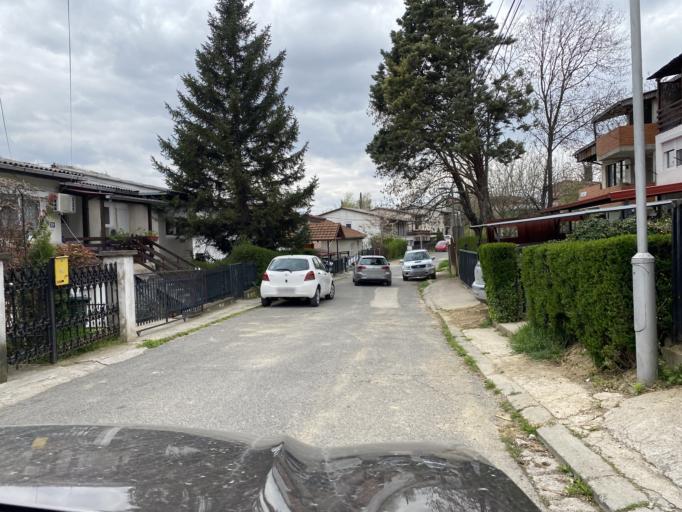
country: MK
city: Radishani
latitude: 42.0595
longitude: 21.4487
